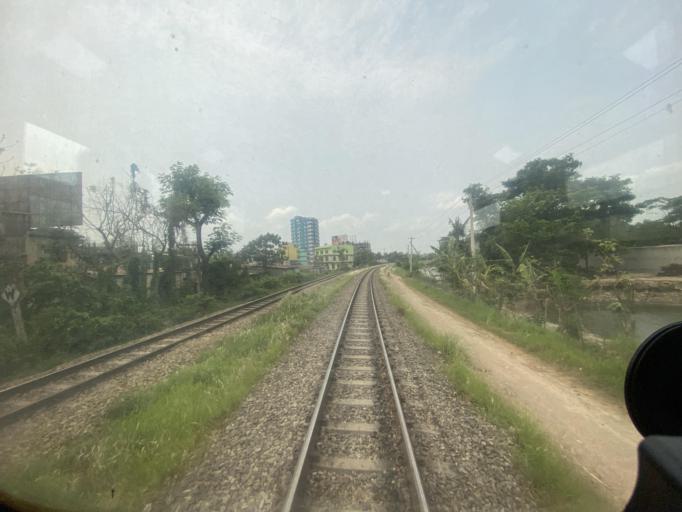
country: BD
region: Chittagong
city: Laksham
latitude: 23.2419
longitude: 91.1239
